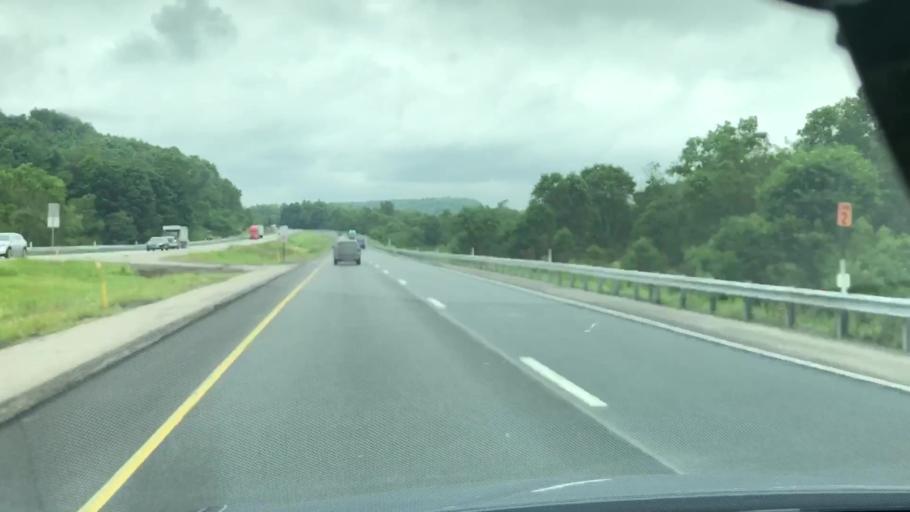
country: US
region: Pennsylvania
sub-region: Butler County
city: Zelienople
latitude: 40.8458
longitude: -80.1026
